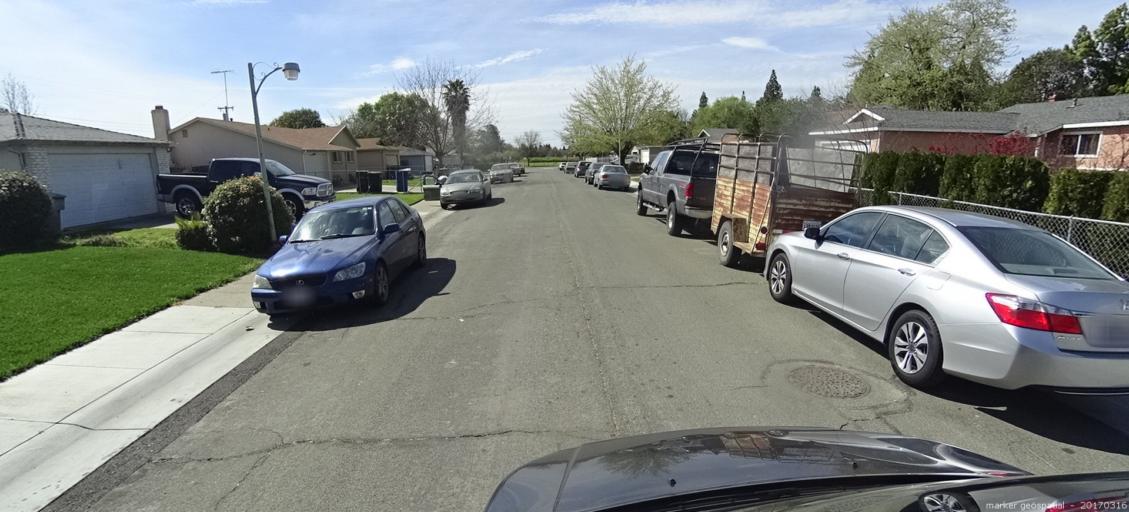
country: US
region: California
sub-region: Sacramento County
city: Parkway
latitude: 38.4794
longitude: -121.4998
